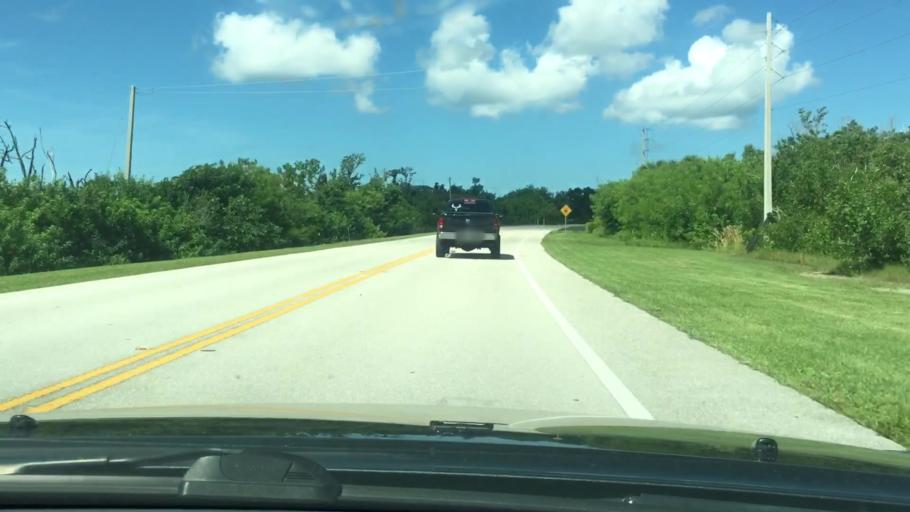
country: US
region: Florida
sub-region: Collier County
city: Marco
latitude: 25.9318
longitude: -81.6722
